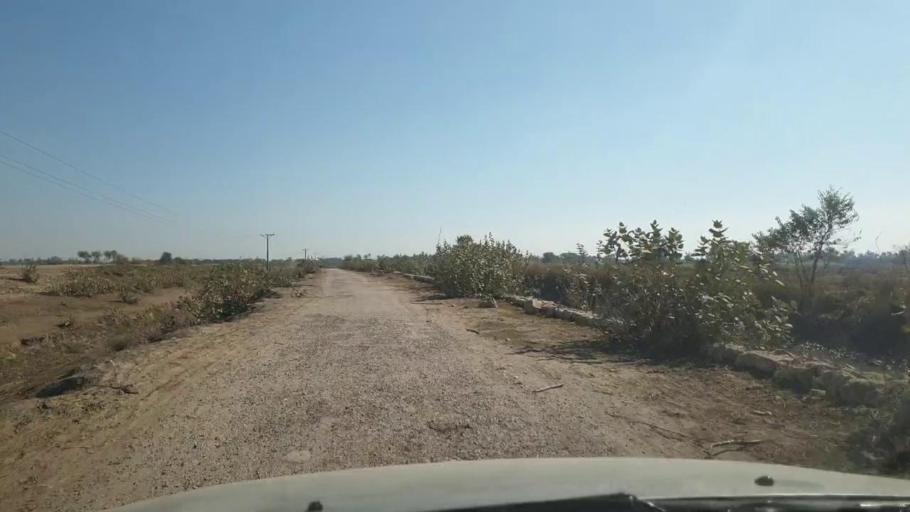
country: PK
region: Sindh
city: Ghotki
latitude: 28.0829
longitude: 69.3427
